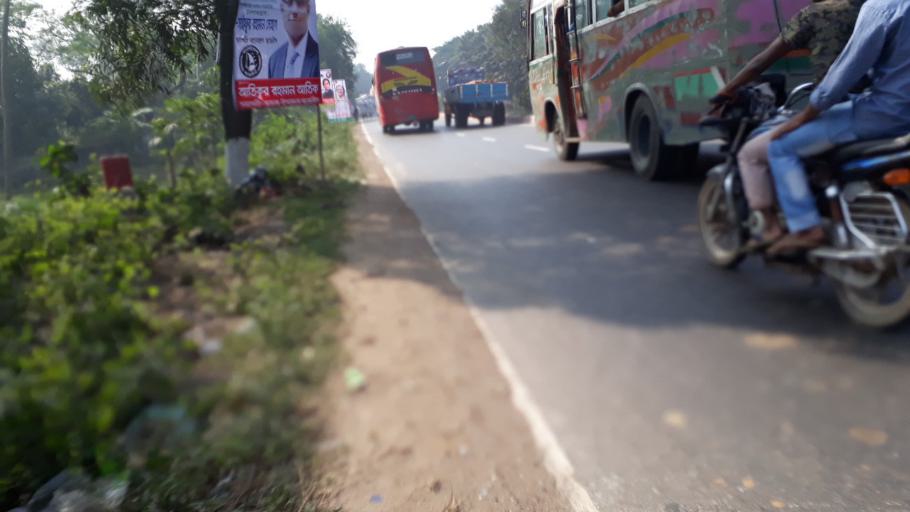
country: BD
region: Dhaka
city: Tungi
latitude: 23.8677
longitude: 90.2718
